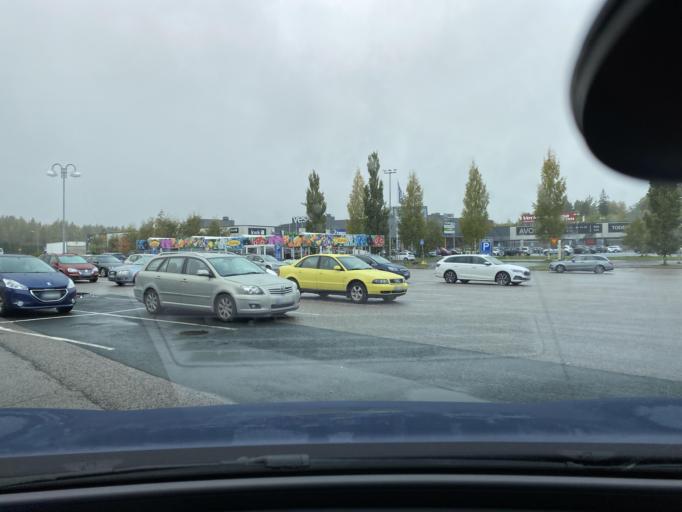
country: FI
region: Pirkanmaa
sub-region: Tampere
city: Tampere
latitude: 61.4663
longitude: 23.7223
